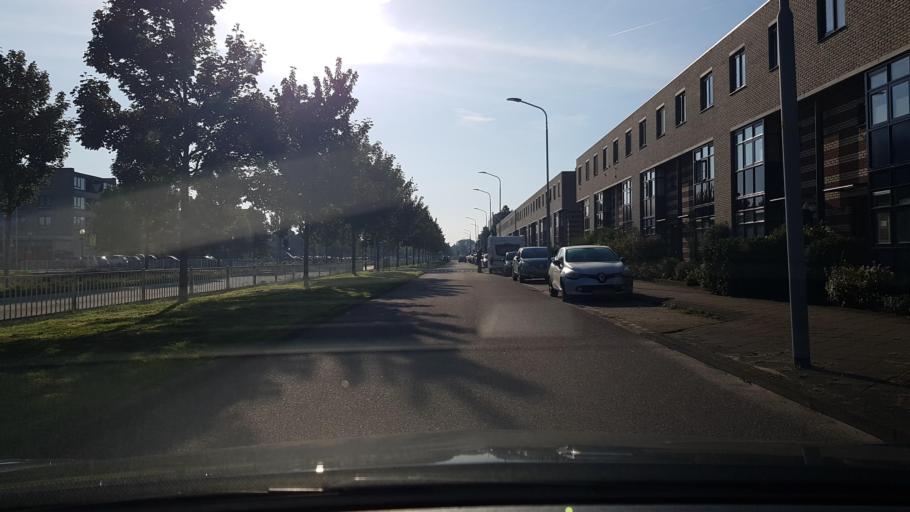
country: NL
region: North Holland
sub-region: Gemeente Haarlemmermeer
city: Hoofddorp
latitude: 52.3015
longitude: 4.6613
